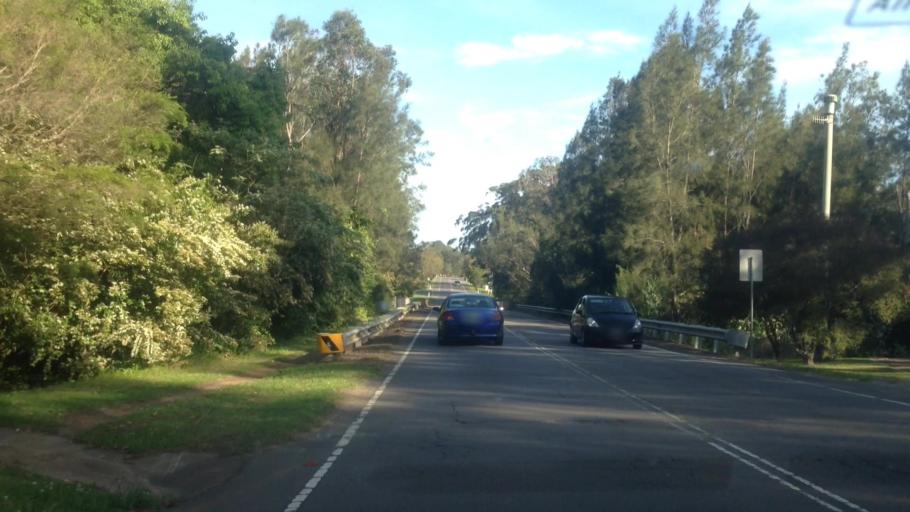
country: AU
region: New South Wales
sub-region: Lake Macquarie Shire
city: Dora Creek
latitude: -33.0995
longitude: 151.4739
